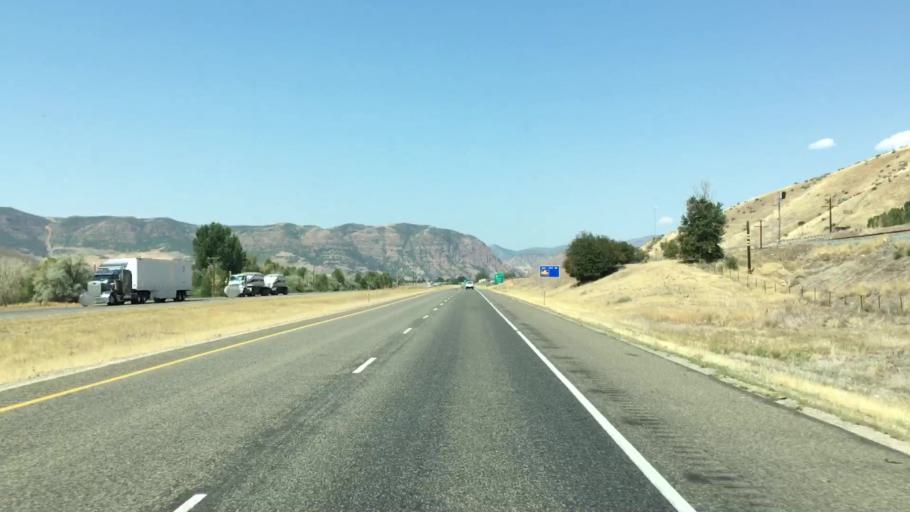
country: US
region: Utah
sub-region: Summit County
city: Coalville
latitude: 41.0024
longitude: -111.4694
